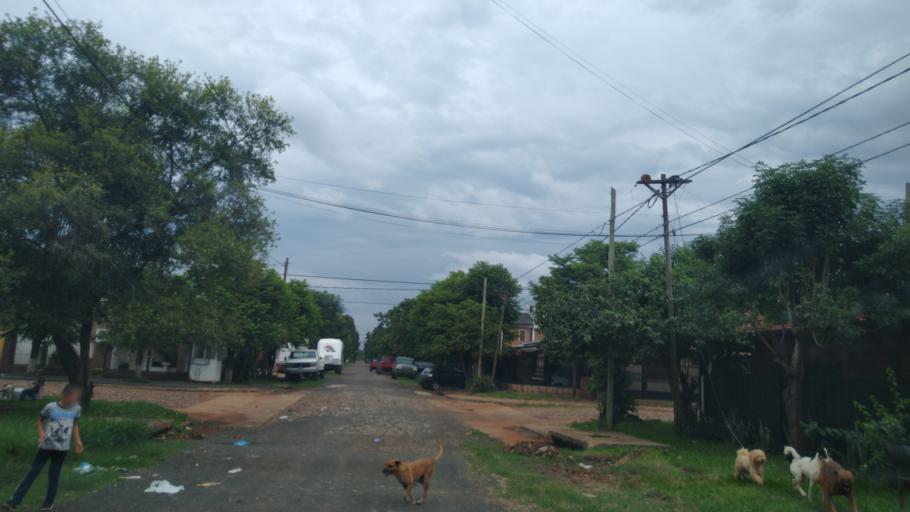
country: AR
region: Misiones
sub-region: Departamento de Capital
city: Posadas
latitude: -27.3767
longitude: -55.9207
